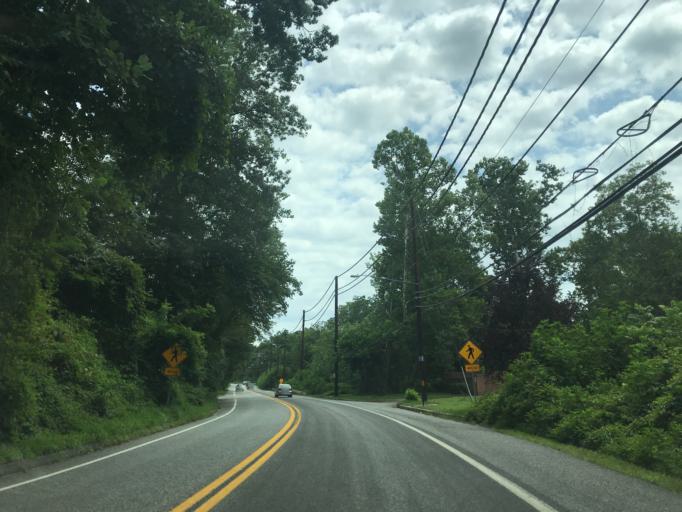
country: US
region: Maryland
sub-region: Montgomery County
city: Bethesda
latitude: 38.9708
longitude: -77.1266
